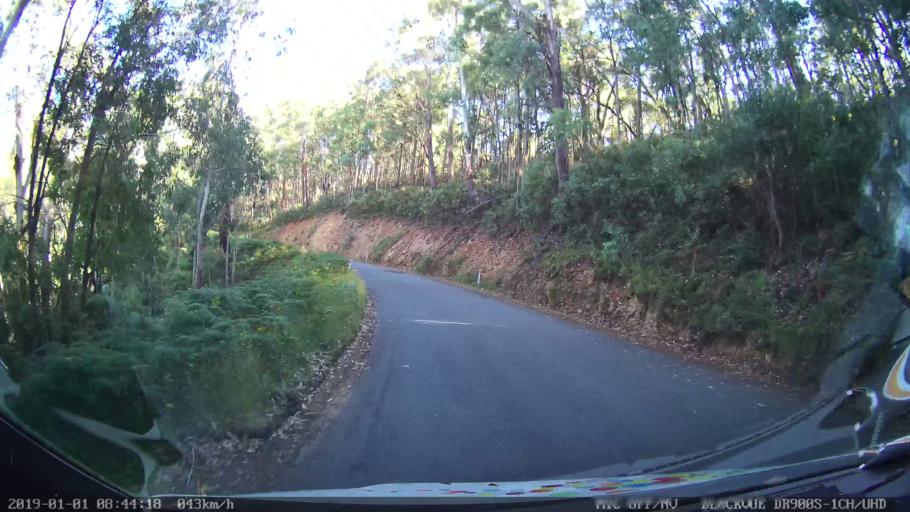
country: AU
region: New South Wales
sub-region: Snowy River
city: Jindabyne
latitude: -36.3116
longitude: 148.1901
